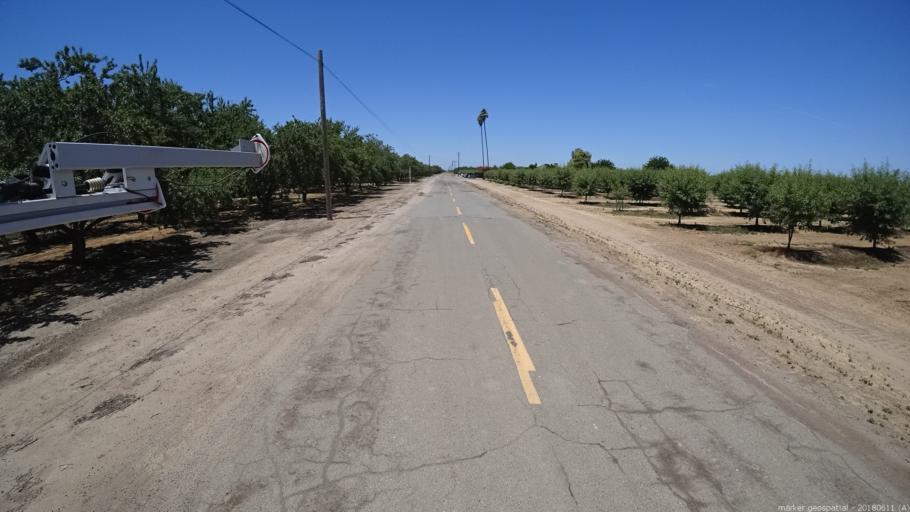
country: US
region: California
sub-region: Madera County
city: Fairmead
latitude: 37.0546
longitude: -120.1945
